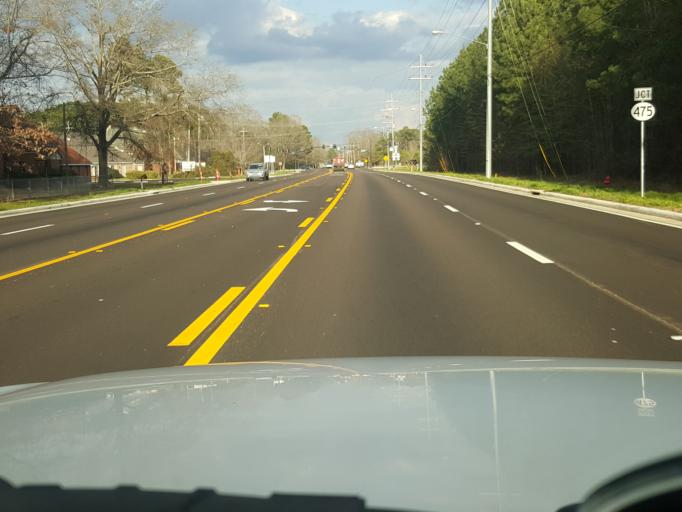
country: US
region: Mississippi
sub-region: Rankin County
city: Flowood
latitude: 32.3283
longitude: -90.0939
